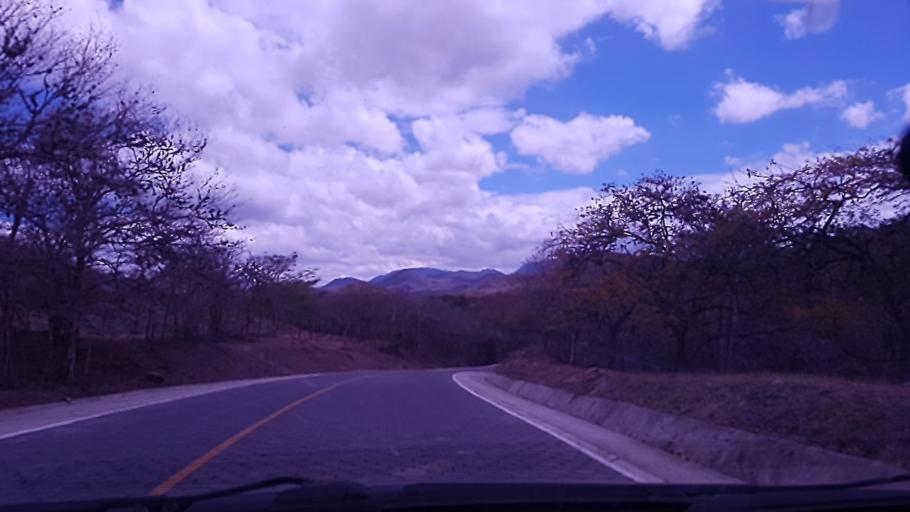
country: NI
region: Esteli
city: Condega
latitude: 13.3721
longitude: -86.3770
